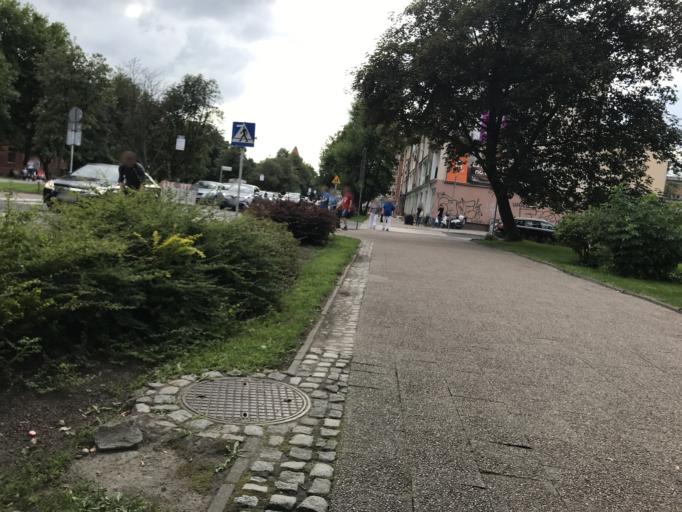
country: PL
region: Pomeranian Voivodeship
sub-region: Gdansk
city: Gdansk
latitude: 54.3539
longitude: 18.6567
